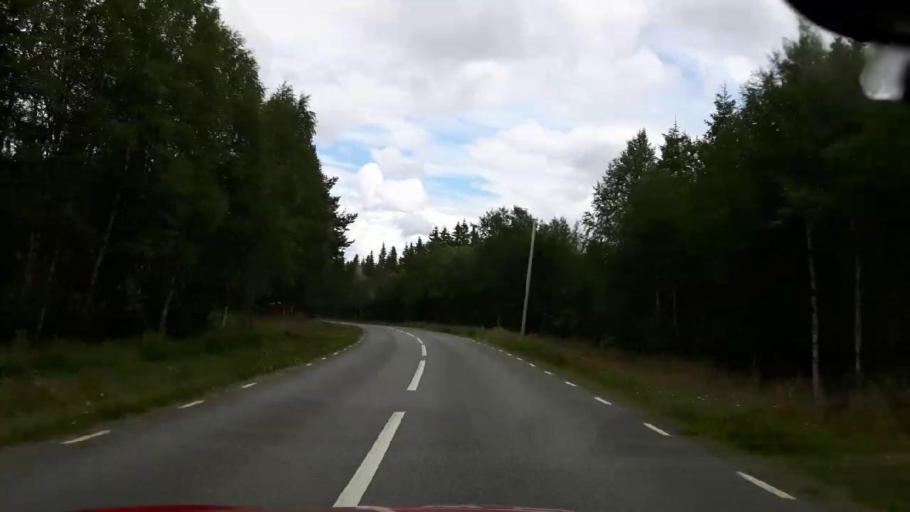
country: NO
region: Nord-Trondelag
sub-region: Lierne
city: Sandvika
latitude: 64.3907
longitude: 14.4729
